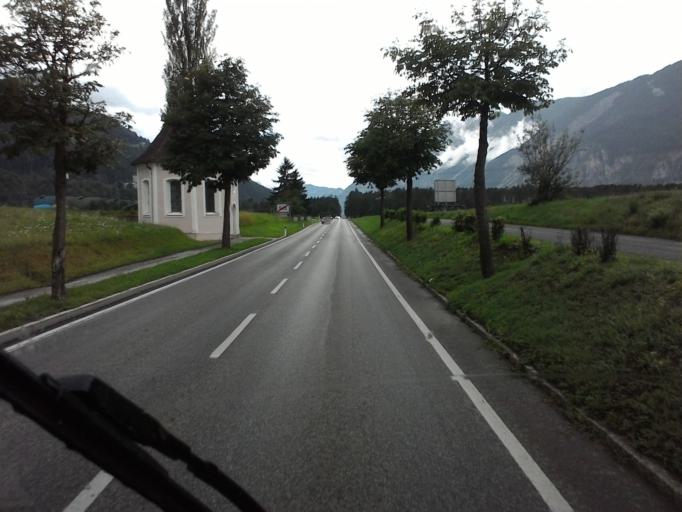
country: AT
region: Tyrol
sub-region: Politischer Bezirk Imst
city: Silz
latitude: 47.2634
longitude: 10.9214
